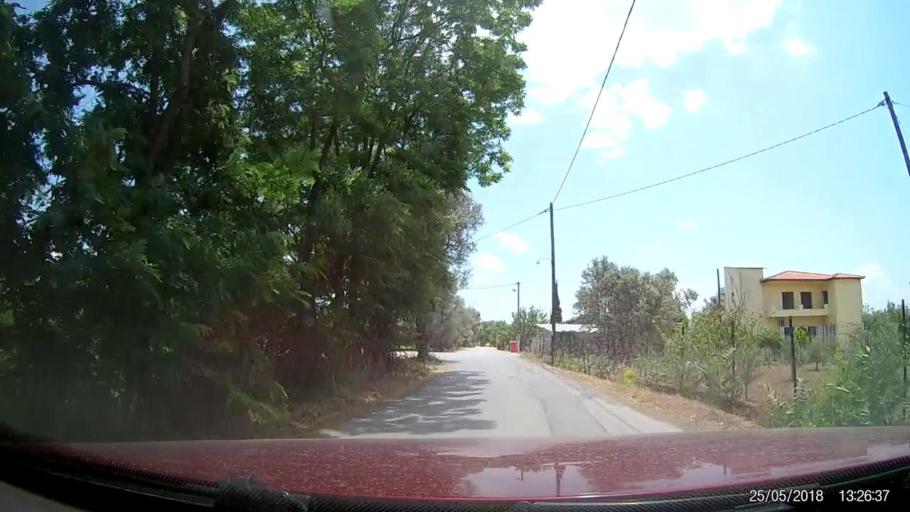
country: GR
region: Central Greece
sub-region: Nomos Evvoias
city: Mytikas
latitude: 38.4551
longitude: 23.6481
